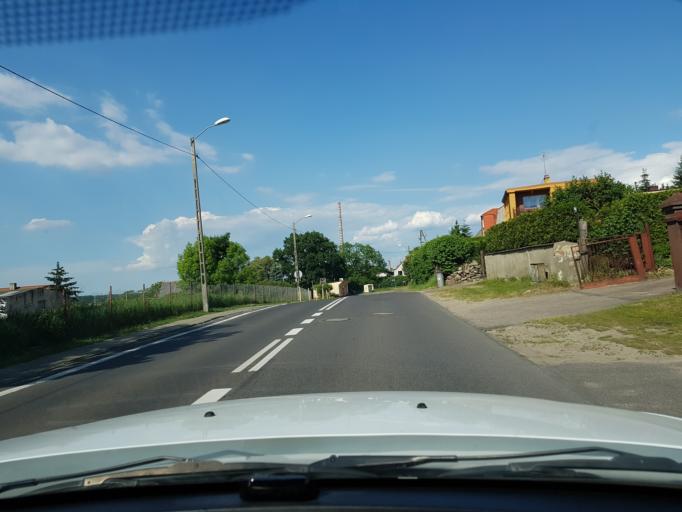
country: PL
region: West Pomeranian Voivodeship
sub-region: Szczecin
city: Szczecin
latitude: 53.3428
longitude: 14.5571
